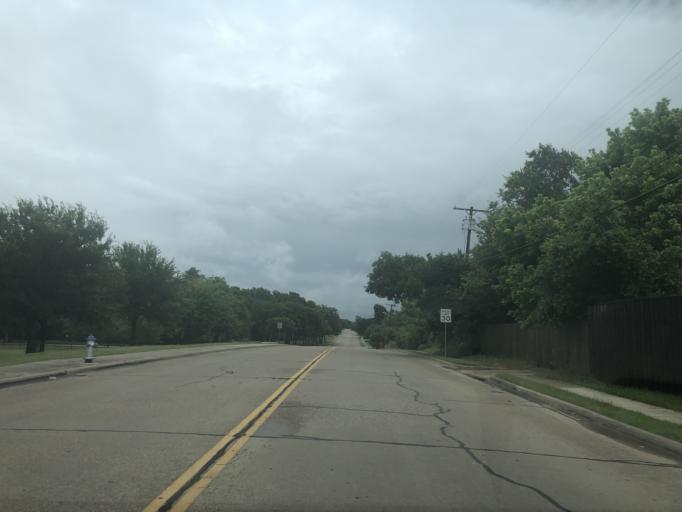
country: US
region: Texas
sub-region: Dallas County
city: Irving
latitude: 32.7939
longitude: -96.9404
